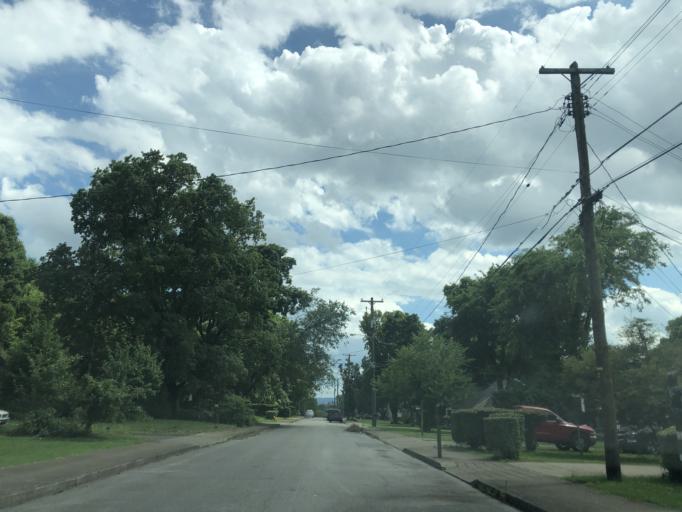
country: US
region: Tennessee
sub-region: Davidson County
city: Nashville
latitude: 36.1975
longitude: -86.7655
